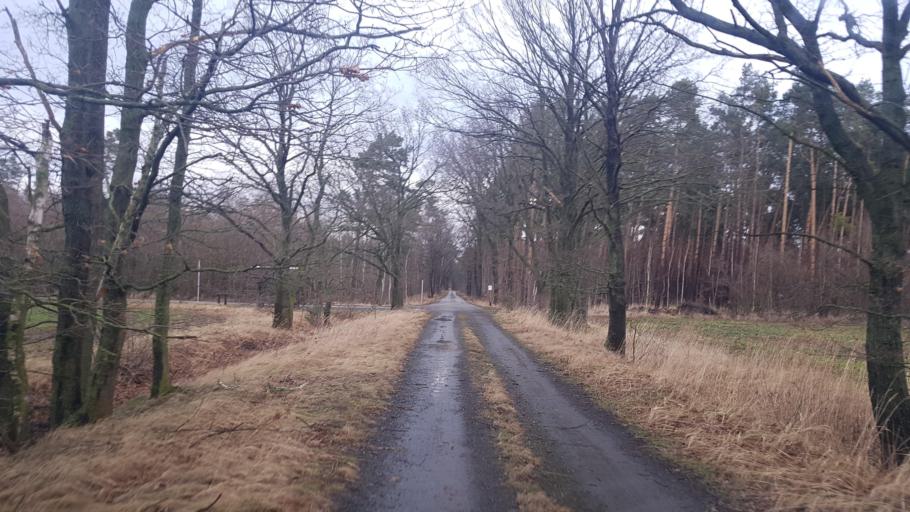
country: DE
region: Brandenburg
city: Plessa
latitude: 51.4350
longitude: 13.6504
